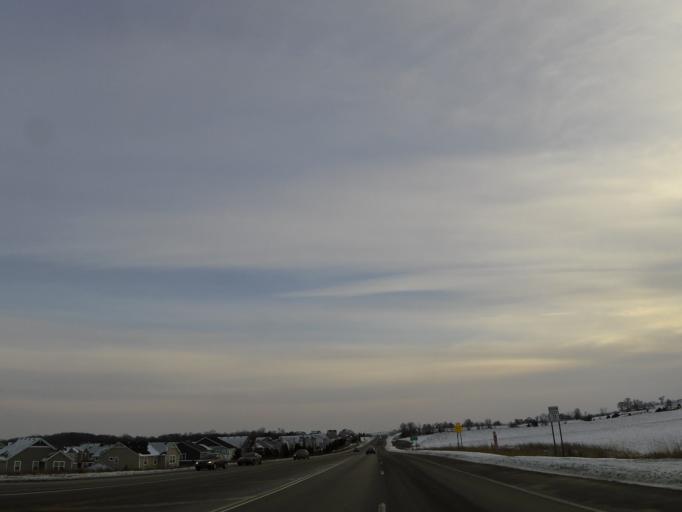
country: US
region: Minnesota
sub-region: Carver County
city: Carver
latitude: 44.7765
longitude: -93.6427
